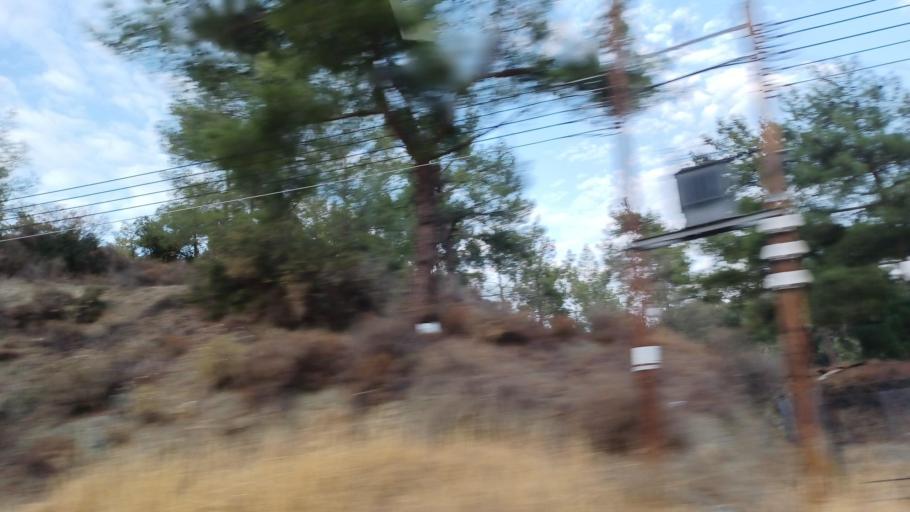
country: CY
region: Limassol
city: Pelendri
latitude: 34.8378
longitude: 32.9559
